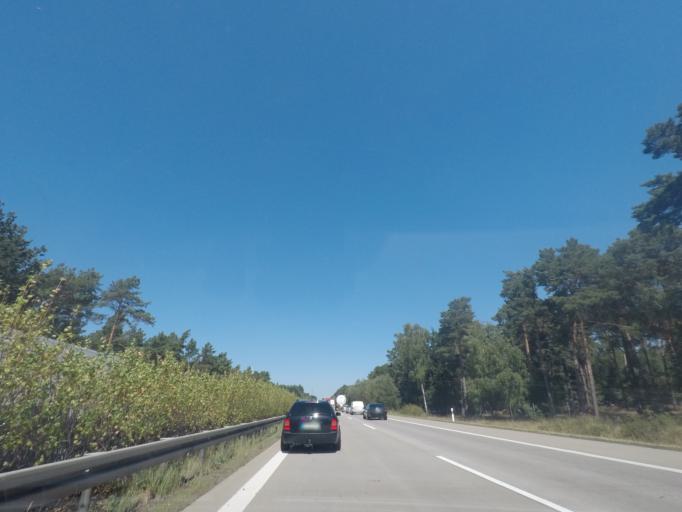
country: DE
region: Brandenburg
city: Bestensee
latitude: 52.2307
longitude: 13.5941
